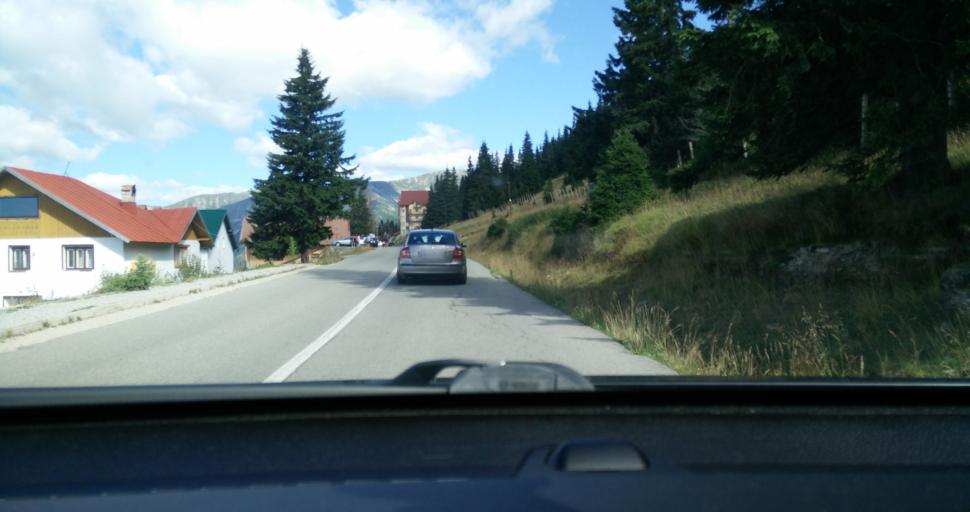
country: RO
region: Gorj
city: Novaci-Straini
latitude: 45.2956
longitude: 23.6844
